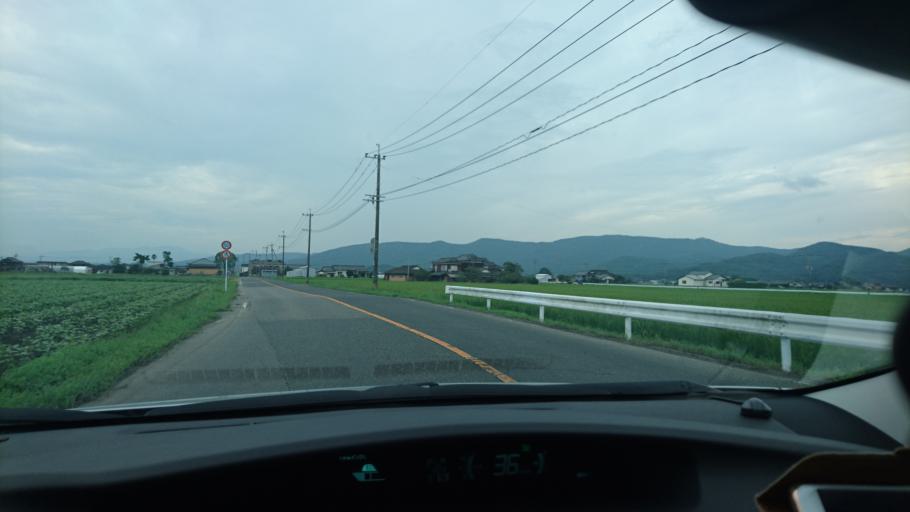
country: JP
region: Saga Prefecture
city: Takeocho-takeo
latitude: 33.1988
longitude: 130.1154
